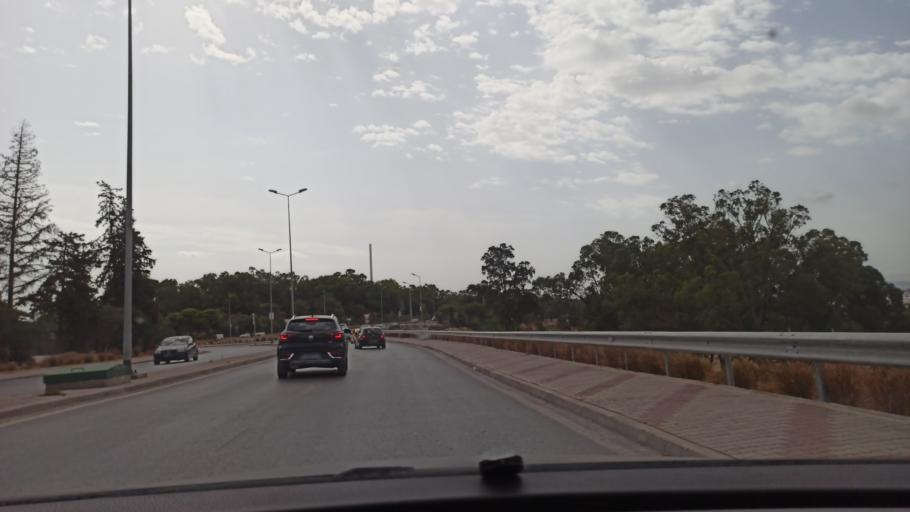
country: TN
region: Tunis
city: Tunis
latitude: 36.8292
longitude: 10.1656
